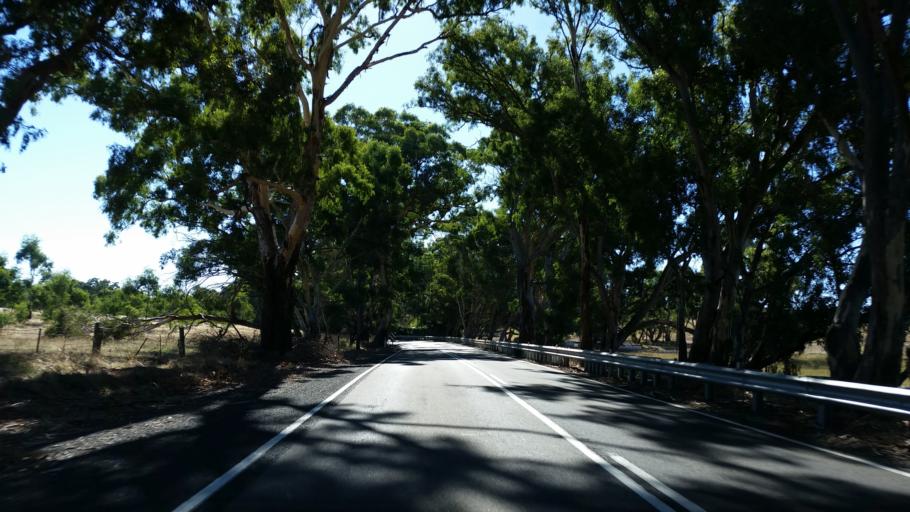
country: AU
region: South Australia
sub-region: Adelaide Hills
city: Birdwood
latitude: -34.8116
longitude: 139.0339
